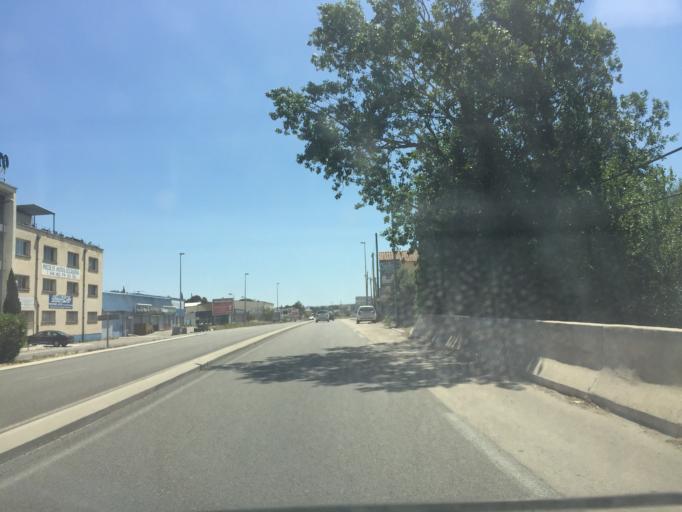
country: FR
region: Provence-Alpes-Cote d'Azur
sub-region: Departement des Bouches-du-Rhone
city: Vitrolles
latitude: 43.4688
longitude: 5.2320
